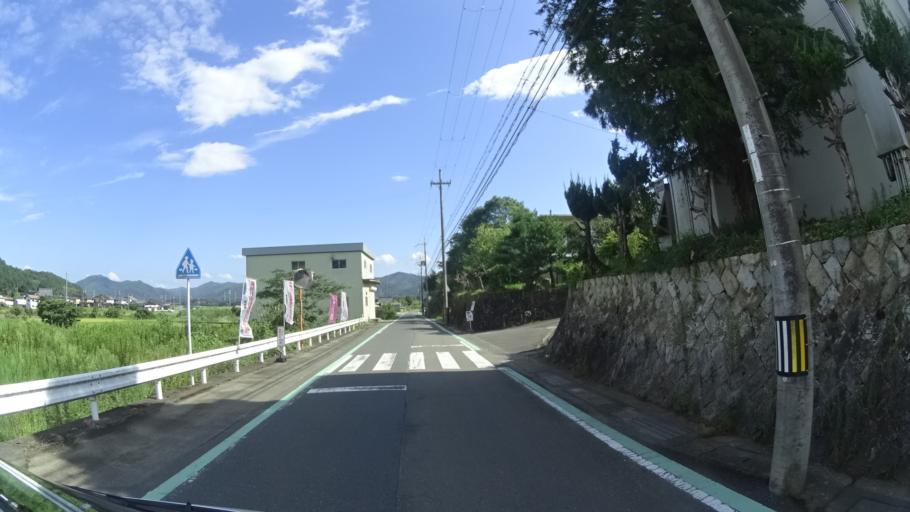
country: JP
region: Kyoto
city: Fukuchiyama
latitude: 35.3203
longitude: 135.1811
